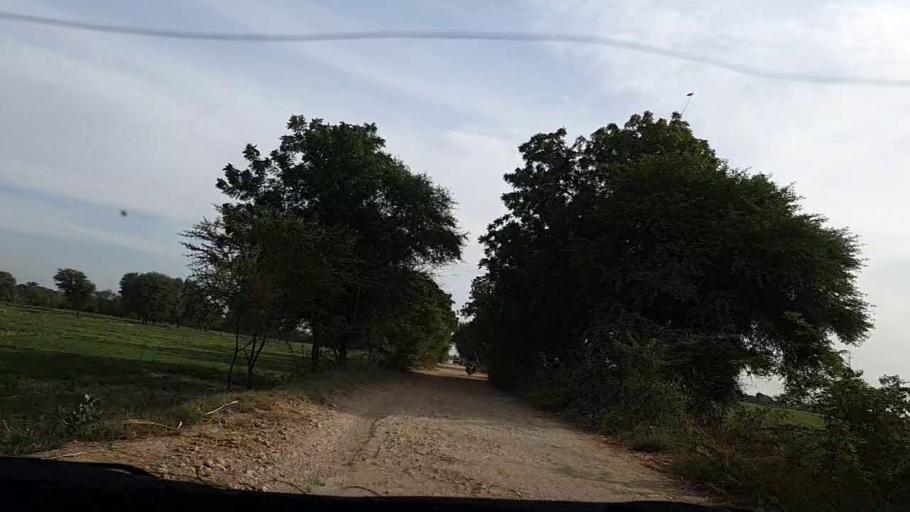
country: PK
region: Sindh
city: Dhoro Naro
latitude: 25.4337
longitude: 69.5221
